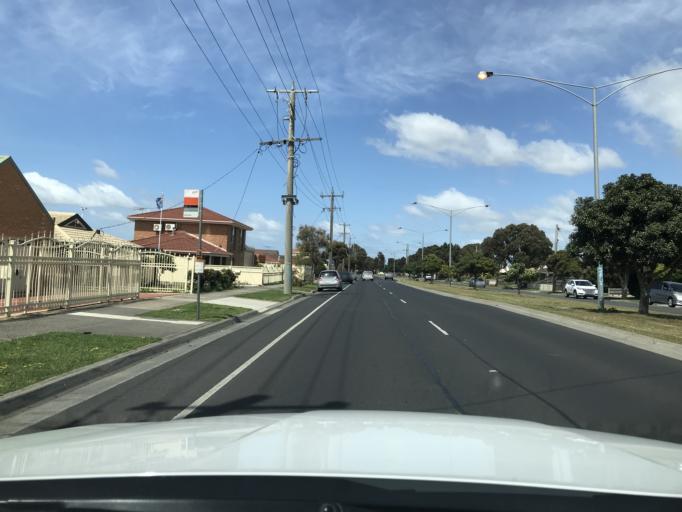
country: AU
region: Victoria
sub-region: Hume
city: Roxburgh Park
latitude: -37.6098
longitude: 144.9280
